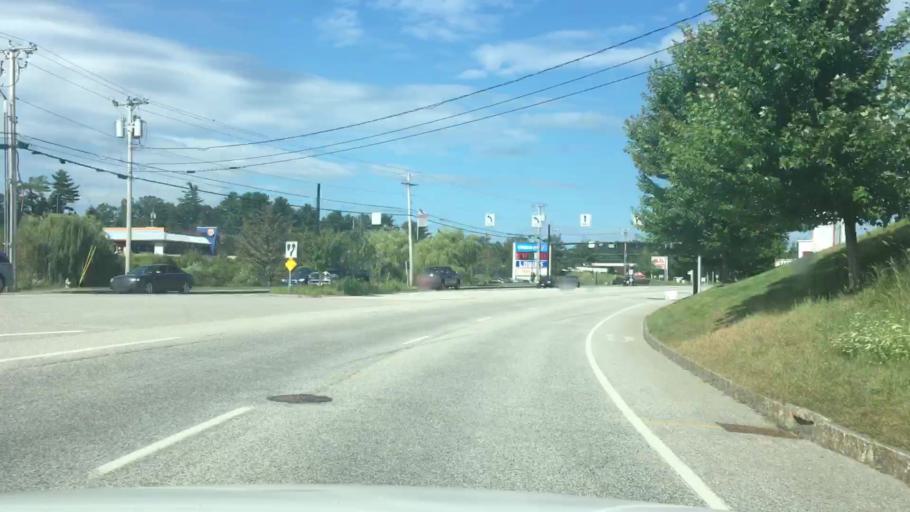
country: US
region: Maine
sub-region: Androscoggin County
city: Auburn
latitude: 44.1203
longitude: -70.2344
